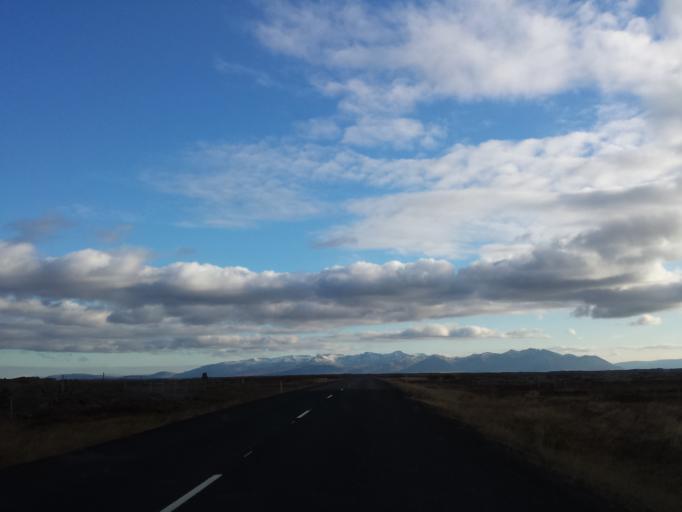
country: IS
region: West
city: Borgarnes
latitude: 64.6821
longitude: -22.0833
